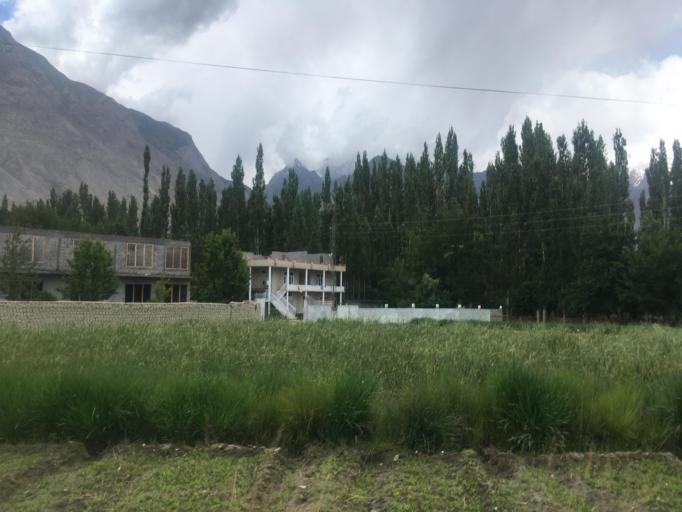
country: PK
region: Gilgit-Baltistan
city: Skardu
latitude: 35.2908
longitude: 75.6161
